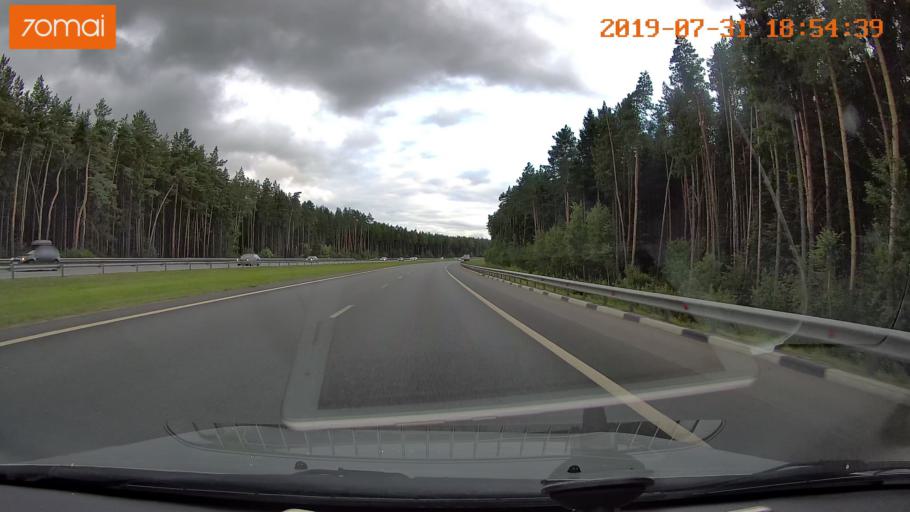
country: RU
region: Moskovskaya
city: Raduzhnyy
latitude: 55.1865
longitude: 38.6691
